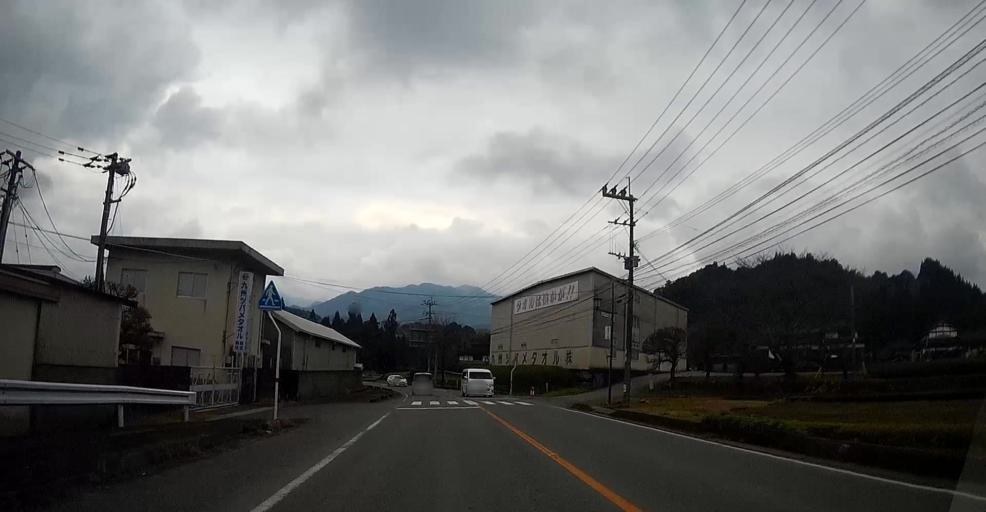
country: JP
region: Kumamoto
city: Matsubase
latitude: 32.6236
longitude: 130.8147
